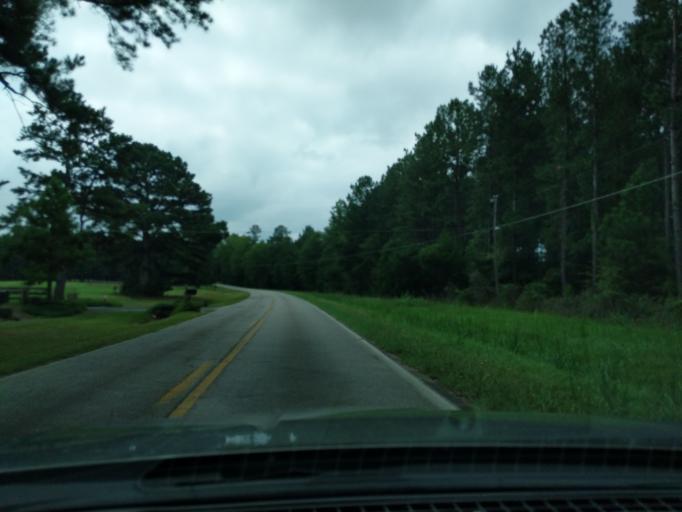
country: US
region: Georgia
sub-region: Columbia County
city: Appling
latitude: 33.5991
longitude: -82.3871
